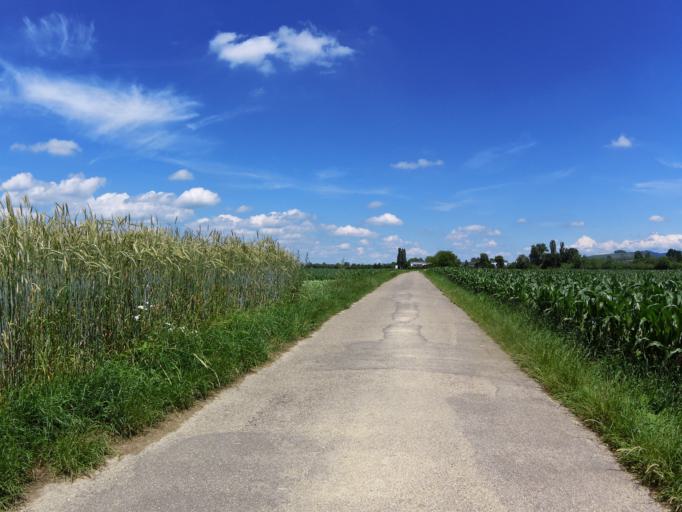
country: DE
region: Baden-Wuerttemberg
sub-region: Freiburg Region
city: Kippenheim
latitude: 48.3250
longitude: 7.8130
